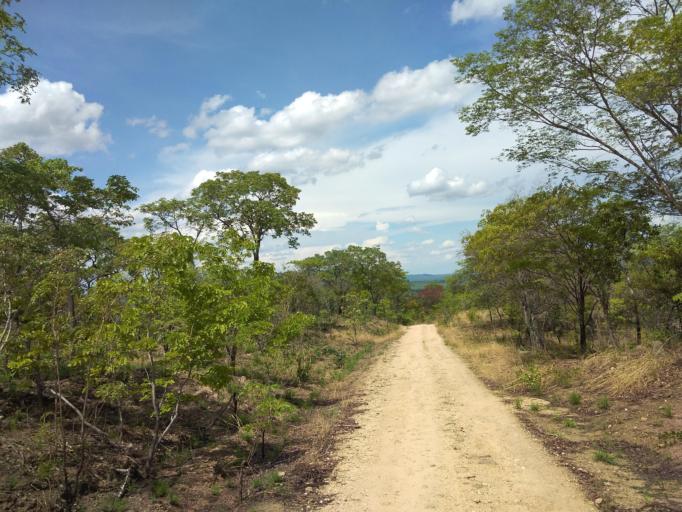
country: ZM
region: Eastern
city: Nyimba
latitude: -14.1195
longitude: 30.1020
